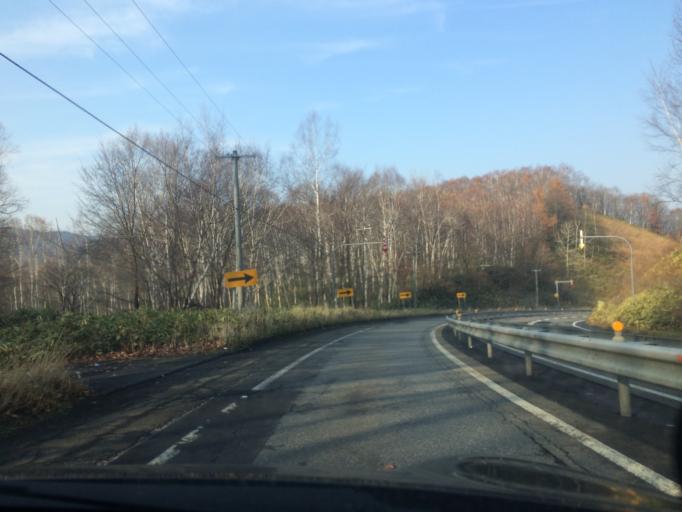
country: JP
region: Hokkaido
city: Shimo-furano
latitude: 42.8844
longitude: 142.2649
